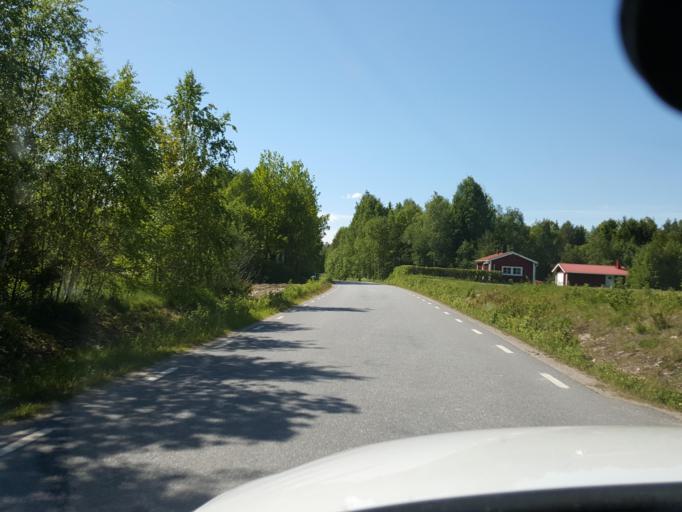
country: SE
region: Gaevleborg
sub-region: Ljusdals Kommun
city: Jaervsoe
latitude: 61.7478
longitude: 16.2615
